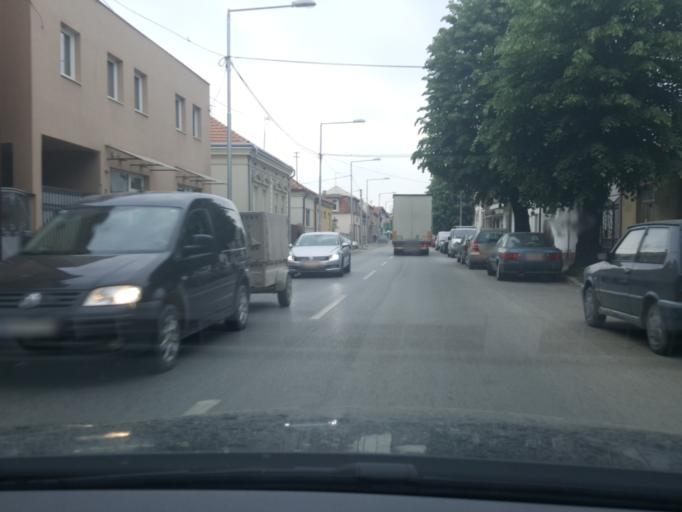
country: RS
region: Central Serbia
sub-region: Kolubarski Okrug
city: Valjevo
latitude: 44.2723
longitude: 19.8801
